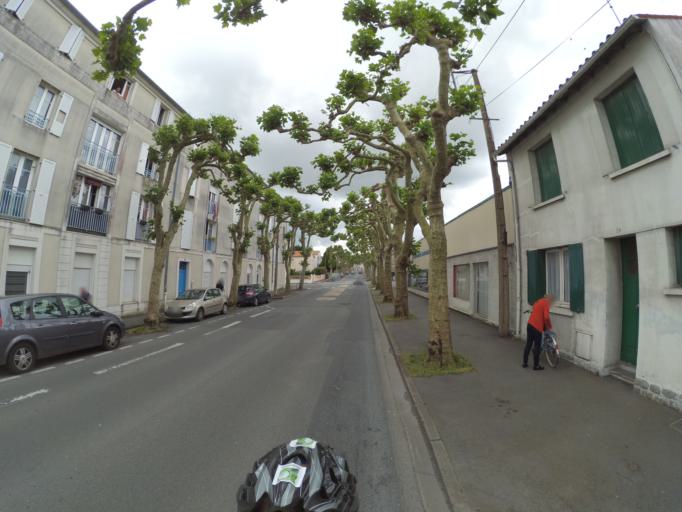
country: FR
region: Poitou-Charentes
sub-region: Departement de la Charente-Maritime
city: Rochefort
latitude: 45.9450
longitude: -0.9620
